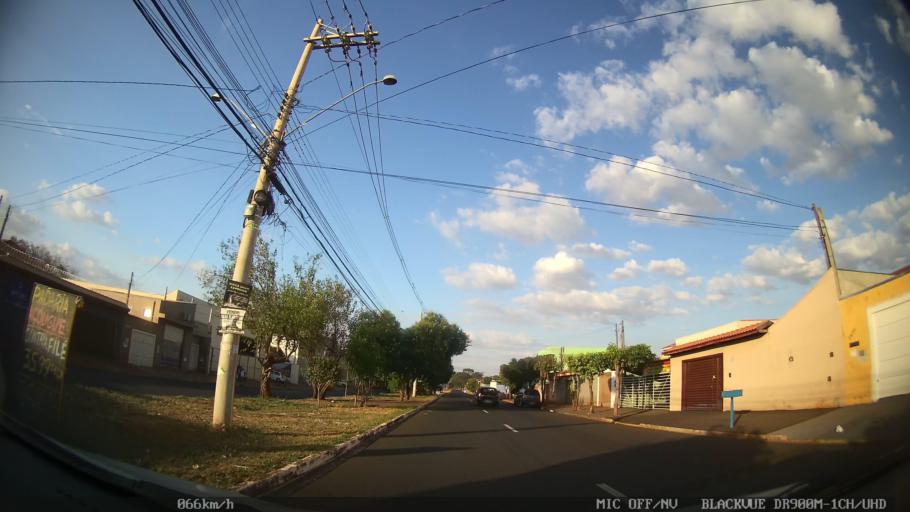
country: BR
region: Sao Paulo
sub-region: Ribeirao Preto
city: Ribeirao Preto
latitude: -21.1612
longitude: -47.7342
